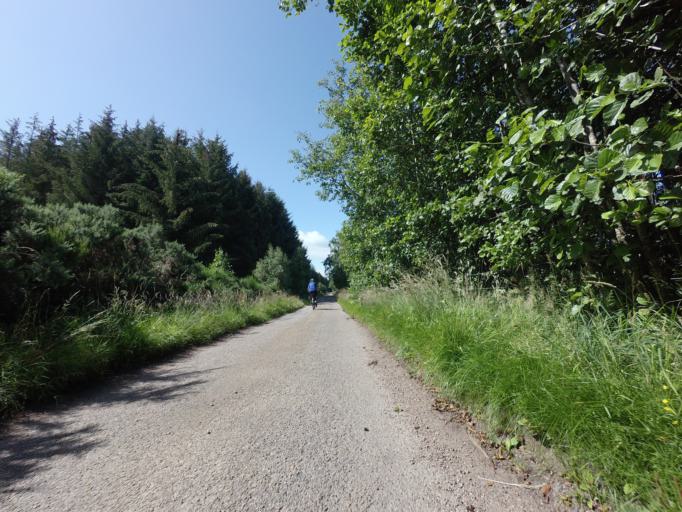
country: GB
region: Scotland
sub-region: Highland
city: Nairn
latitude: 57.5103
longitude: -3.8923
